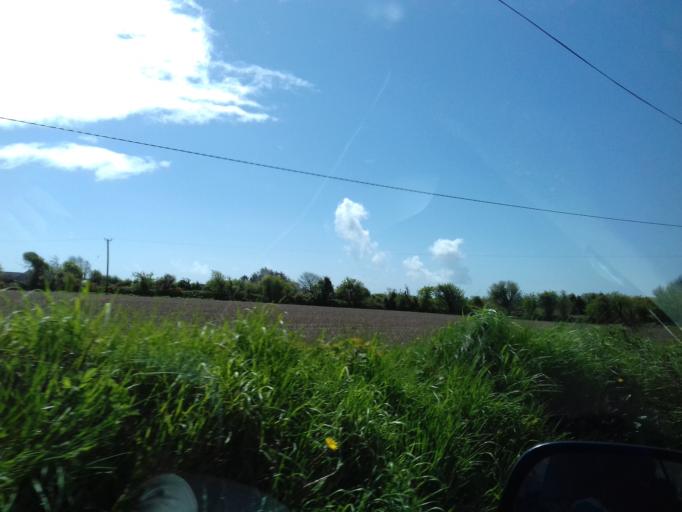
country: IE
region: Munster
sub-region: Waterford
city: Dunmore East
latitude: 52.2379
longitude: -6.8551
